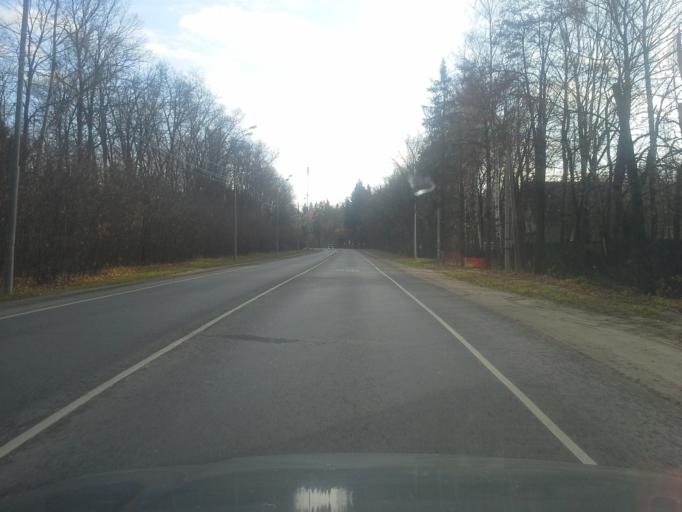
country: RU
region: Moskovskaya
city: Zvenigorod
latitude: 55.6798
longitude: 36.9141
